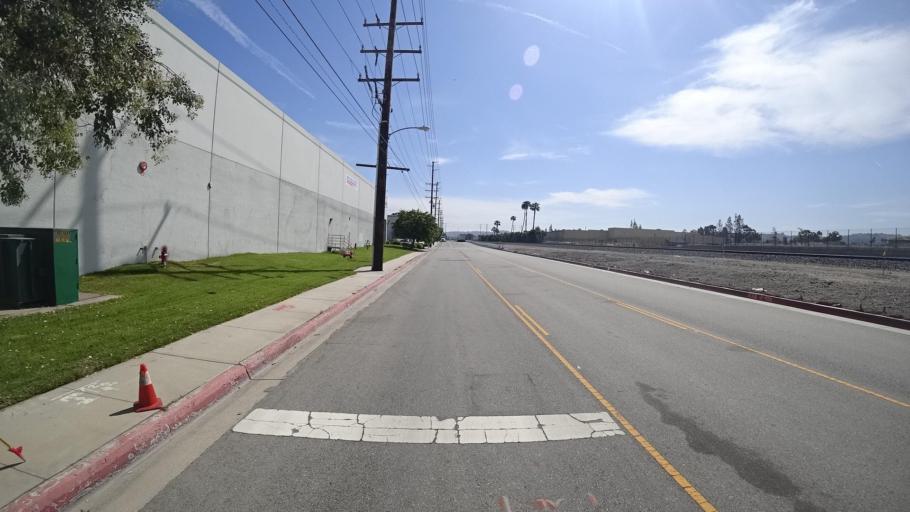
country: US
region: California
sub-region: Los Angeles County
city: South San Jose Hills
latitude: 33.9976
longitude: -117.8931
